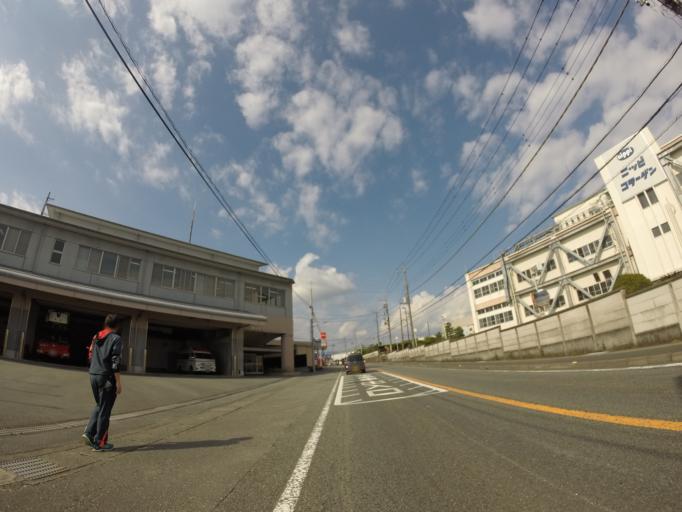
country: JP
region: Shizuoka
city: Fujinomiya
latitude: 35.2199
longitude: 138.6211
